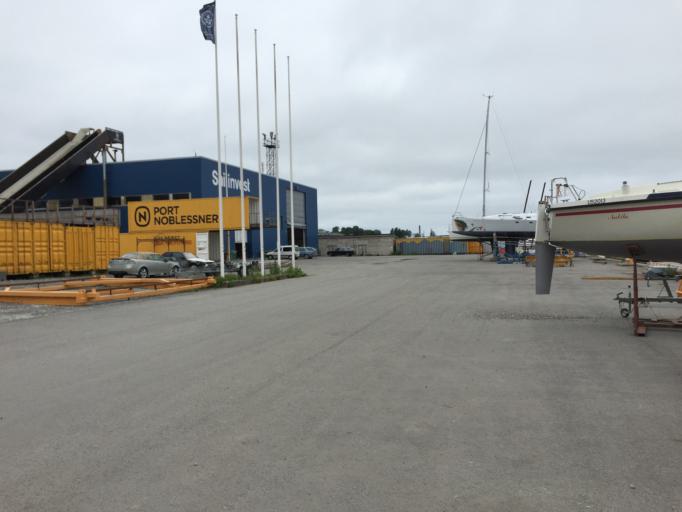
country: EE
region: Harju
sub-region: Tallinna linn
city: Tallinn
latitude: 59.4521
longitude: 24.7297
